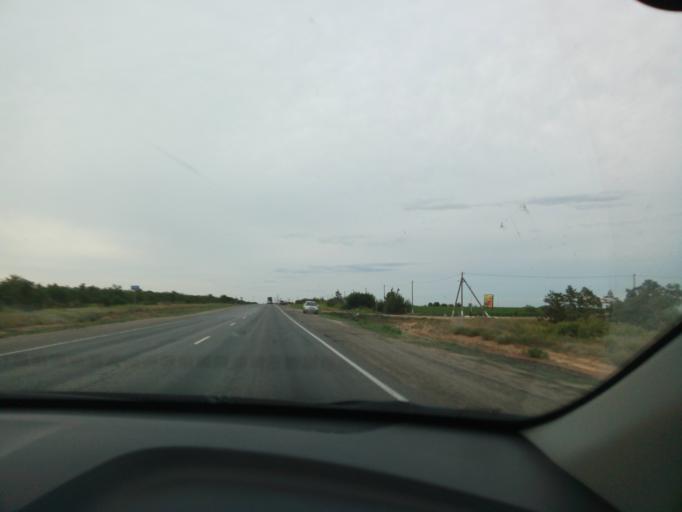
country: RU
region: Volgograd
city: Dubovka
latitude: 49.0386
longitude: 44.7663
